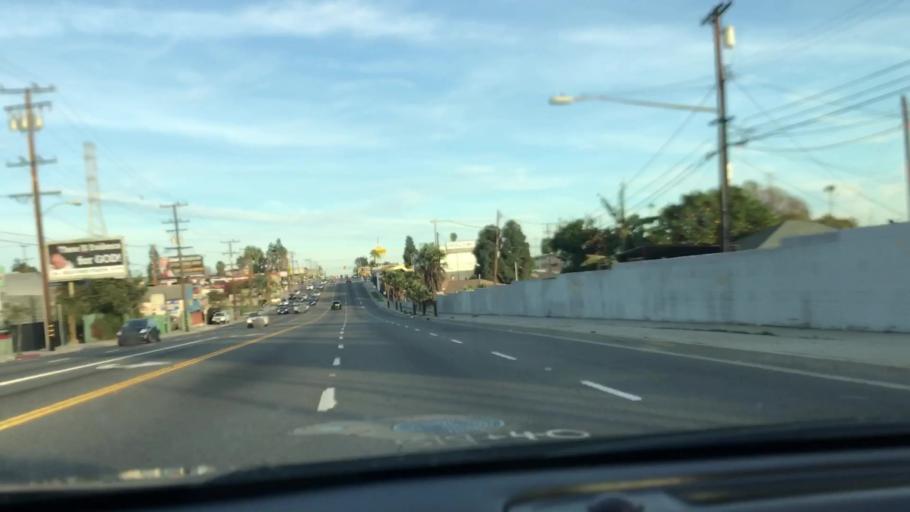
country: US
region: California
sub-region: Los Angeles County
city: West Athens
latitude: 33.9164
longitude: -118.2960
